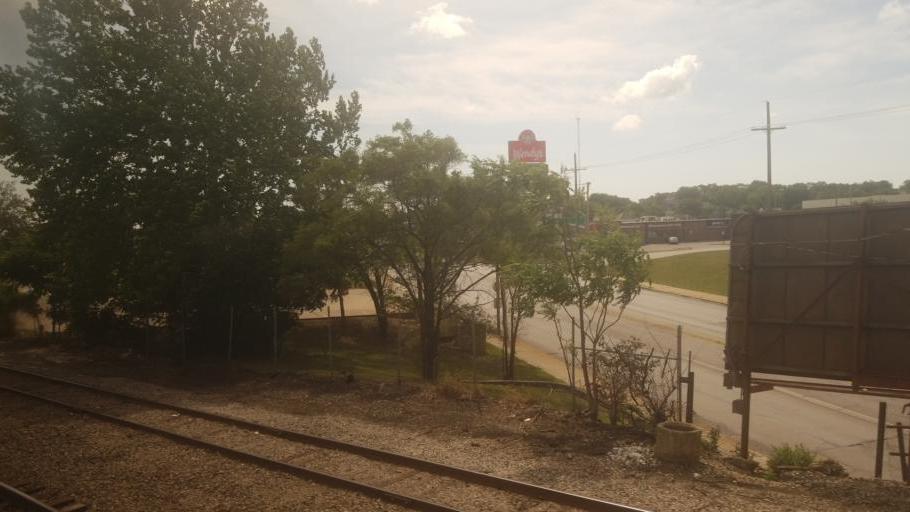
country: US
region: Missouri
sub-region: Jackson County
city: Kansas City
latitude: 39.0944
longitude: -94.5390
